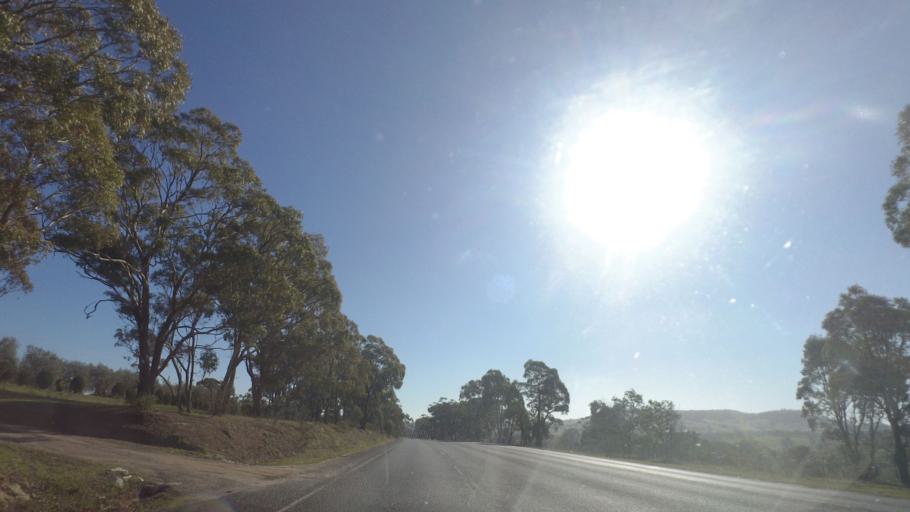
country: AU
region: Victoria
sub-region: Mount Alexander
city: Castlemaine
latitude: -37.0576
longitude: 144.2953
